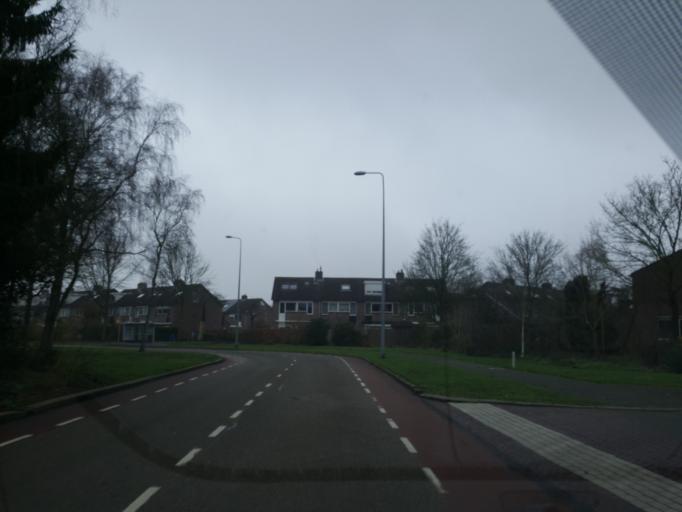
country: NL
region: North Holland
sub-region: Gemeente Bussum
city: Bussum
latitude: 52.2673
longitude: 5.1390
